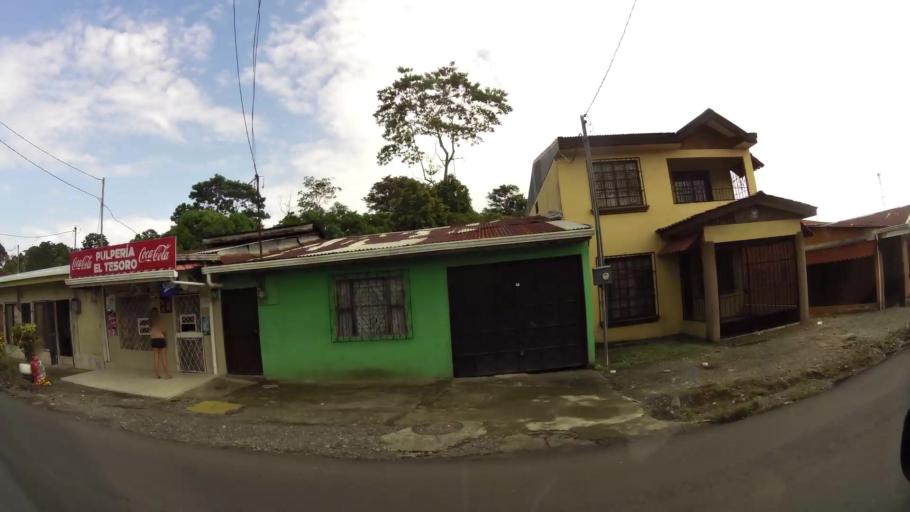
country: CR
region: Limon
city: Limon
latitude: 9.9871
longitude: -83.0481
